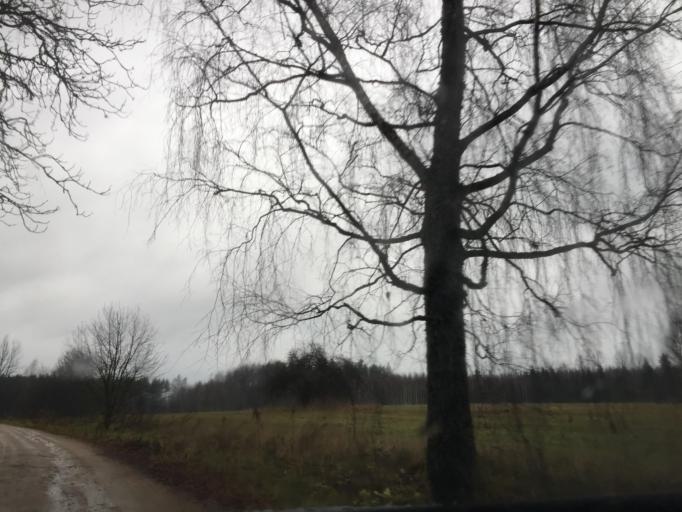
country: LV
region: Limbazu Rajons
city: Limbazi
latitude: 57.5489
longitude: 24.7630
